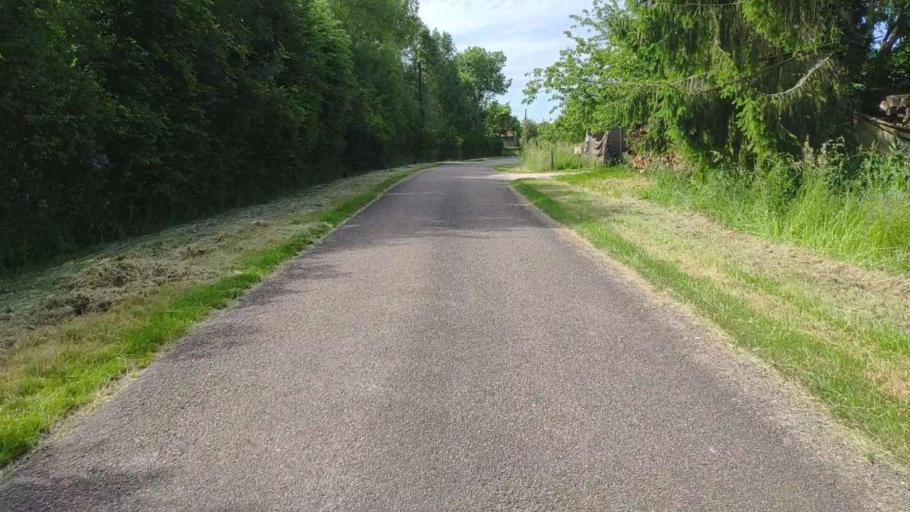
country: FR
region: Franche-Comte
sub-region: Departement du Jura
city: Bletterans
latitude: 46.7110
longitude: 5.4575
